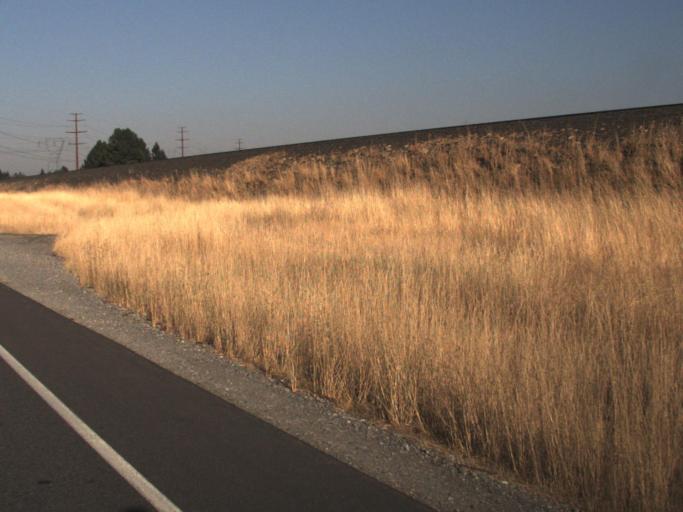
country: US
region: Washington
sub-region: Spokane County
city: Otis Orchards-East Farms
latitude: 47.7160
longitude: -117.0876
